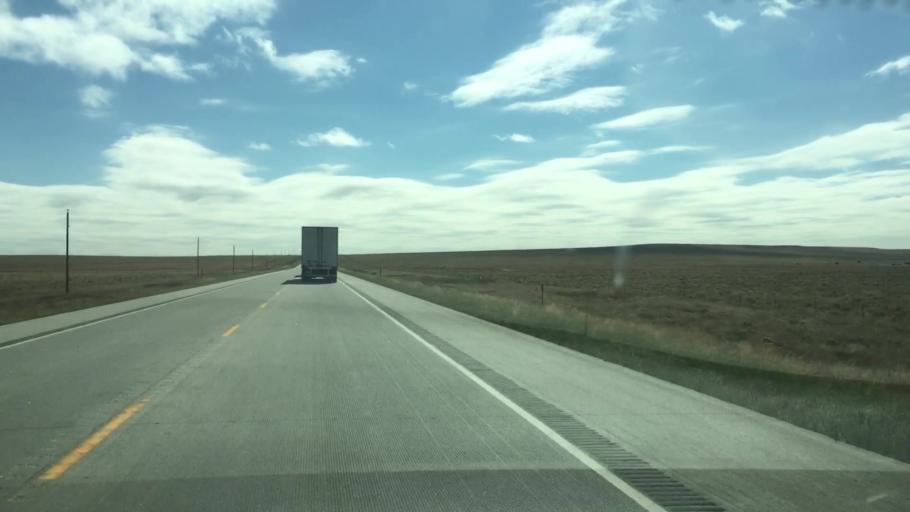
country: US
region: Colorado
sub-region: Lincoln County
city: Hugo
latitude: 39.0309
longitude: -103.3246
